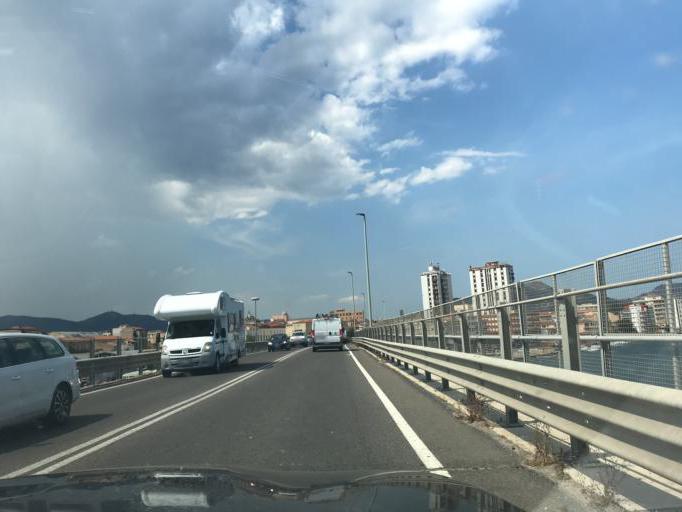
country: IT
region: Sardinia
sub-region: Provincia di Olbia-Tempio
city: Olbia
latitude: 40.9185
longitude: 9.5015
